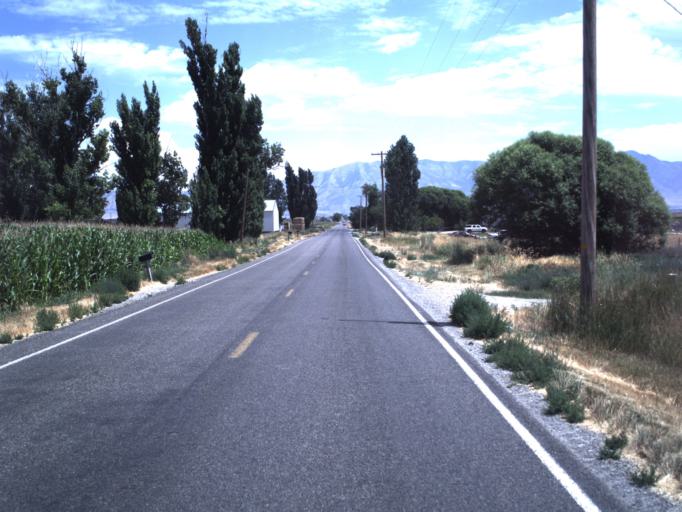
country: US
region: Utah
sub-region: Box Elder County
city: Tremonton
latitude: 41.6944
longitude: -112.2908
